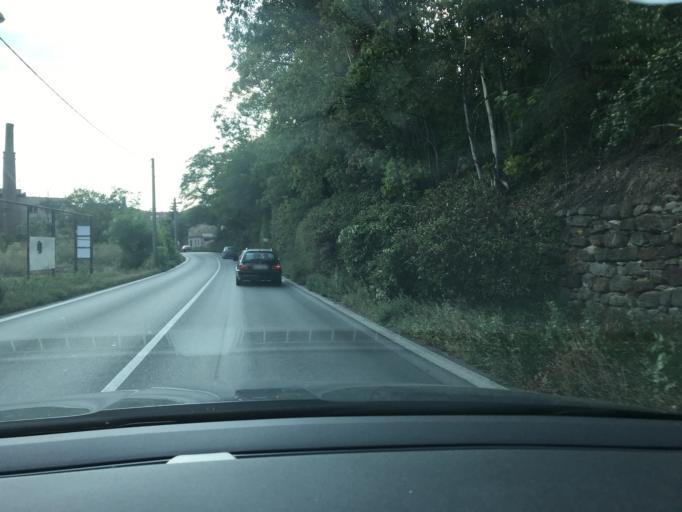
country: CZ
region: Central Bohemia
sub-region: Okres Kladno
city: Slany
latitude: 50.2348
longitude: 14.0943
